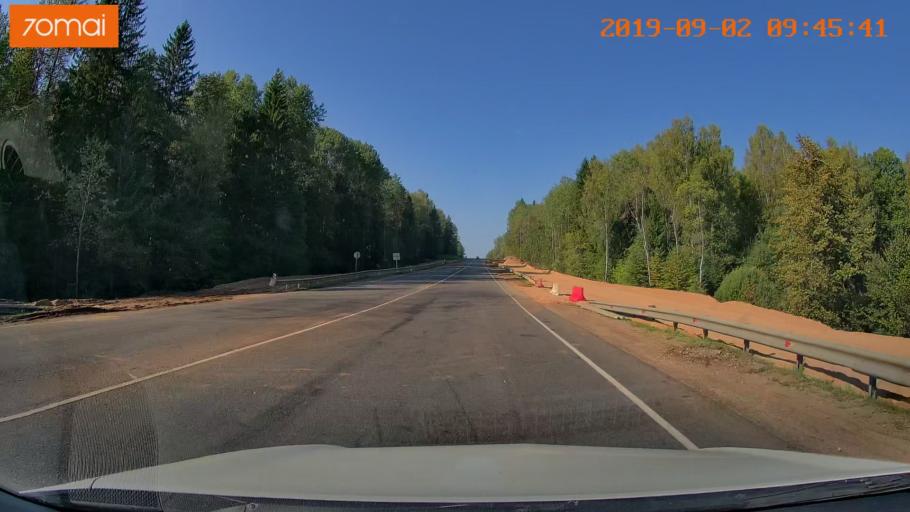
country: RU
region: Kaluga
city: Mosal'sk
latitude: 54.6339
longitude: 34.8447
